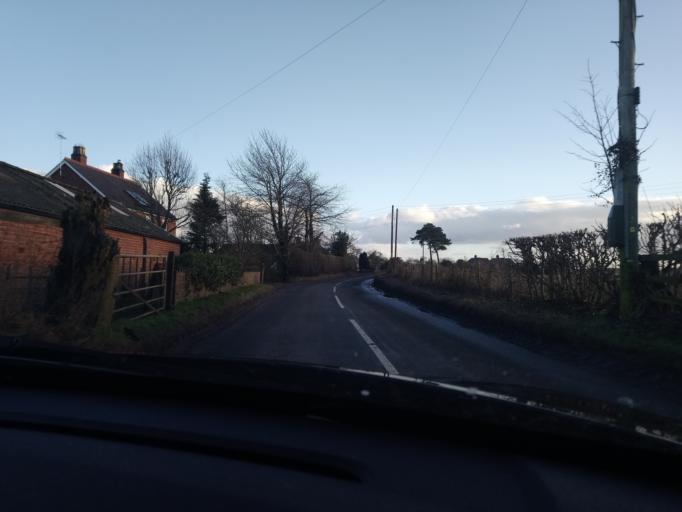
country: GB
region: England
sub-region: Shropshire
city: Petton
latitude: 52.8902
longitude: -2.7925
